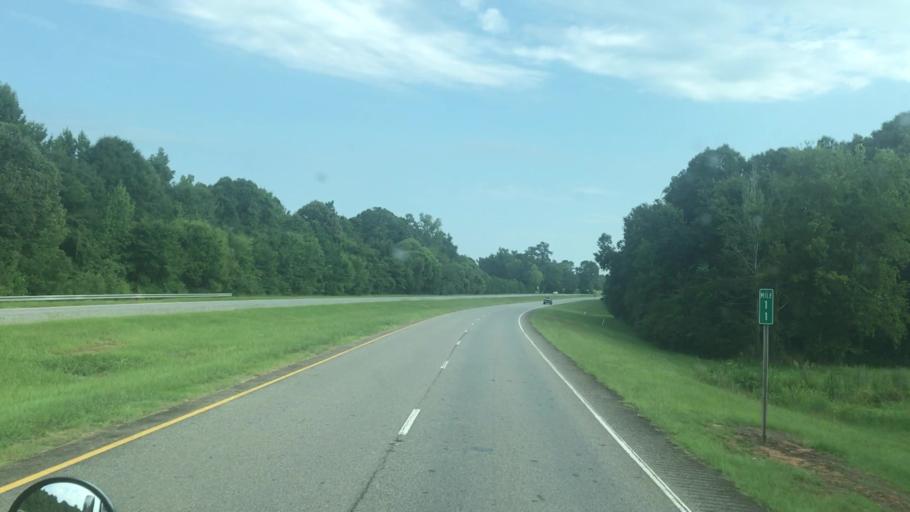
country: US
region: Georgia
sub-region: Early County
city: Blakely
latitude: 31.3702
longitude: -84.9209
